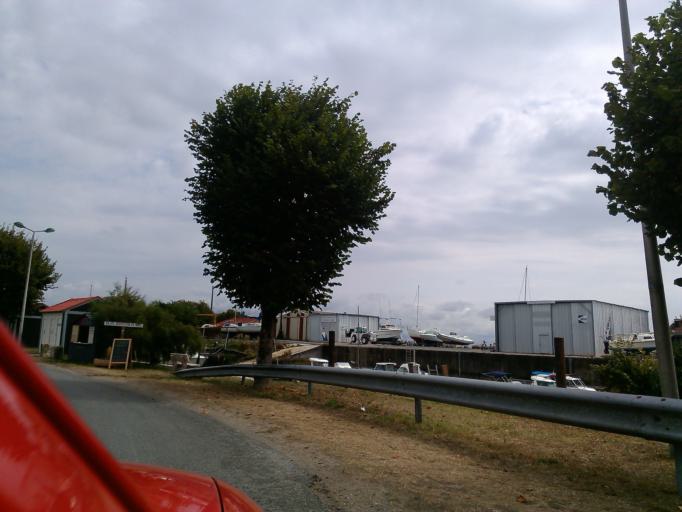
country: FR
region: Poitou-Charentes
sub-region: Departement de la Charente-Maritime
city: La Tremblade
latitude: 45.7675
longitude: -1.1360
